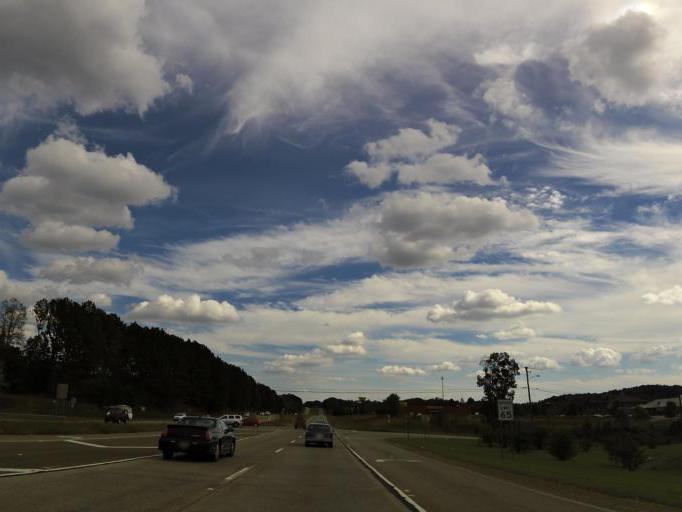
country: US
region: Georgia
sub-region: Pickens County
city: Nelson
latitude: 34.4016
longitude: -84.4173
